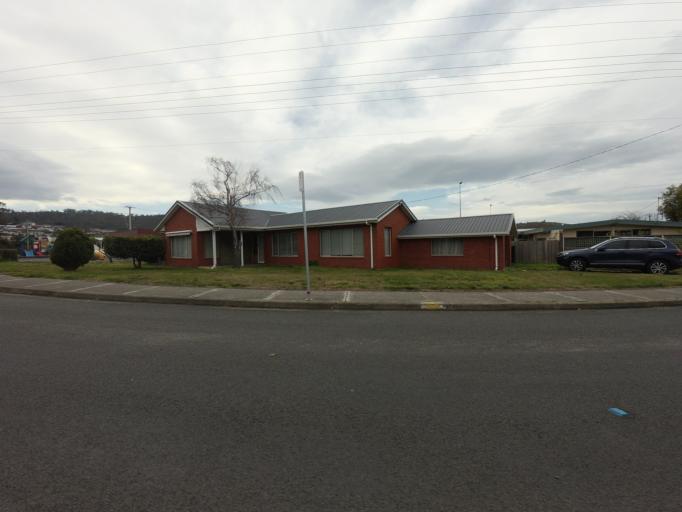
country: AU
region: Tasmania
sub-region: Clarence
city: Howrah
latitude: -42.8775
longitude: 147.3909
